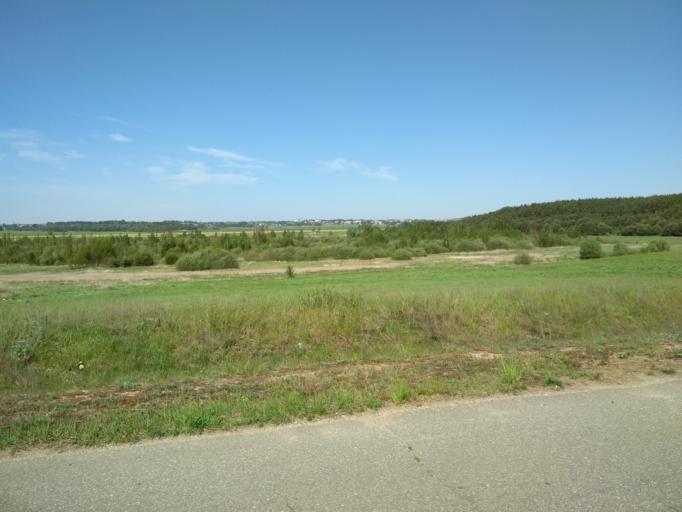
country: BY
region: Grodnenskaya
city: Mir
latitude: 53.3879
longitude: 26.3629
